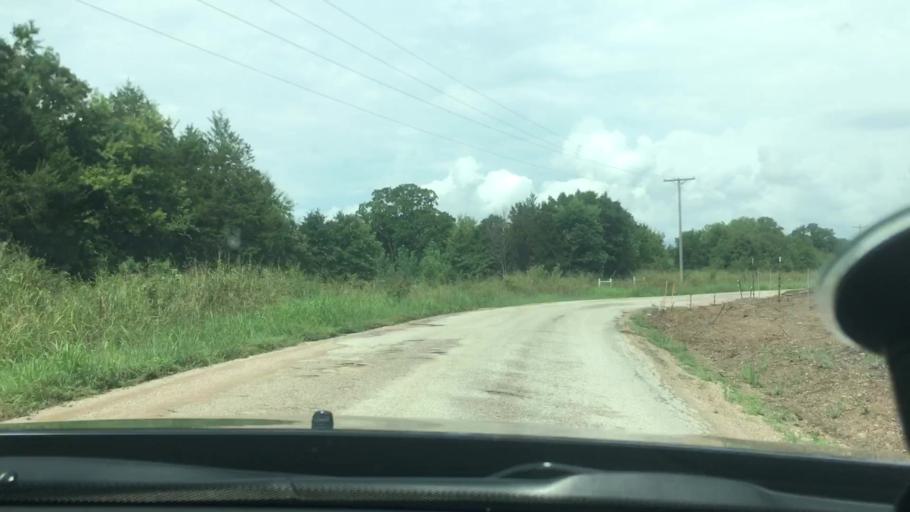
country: US
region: Oklahoma
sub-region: Carter County
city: Dickson
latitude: 34.2414
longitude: -96.9167
